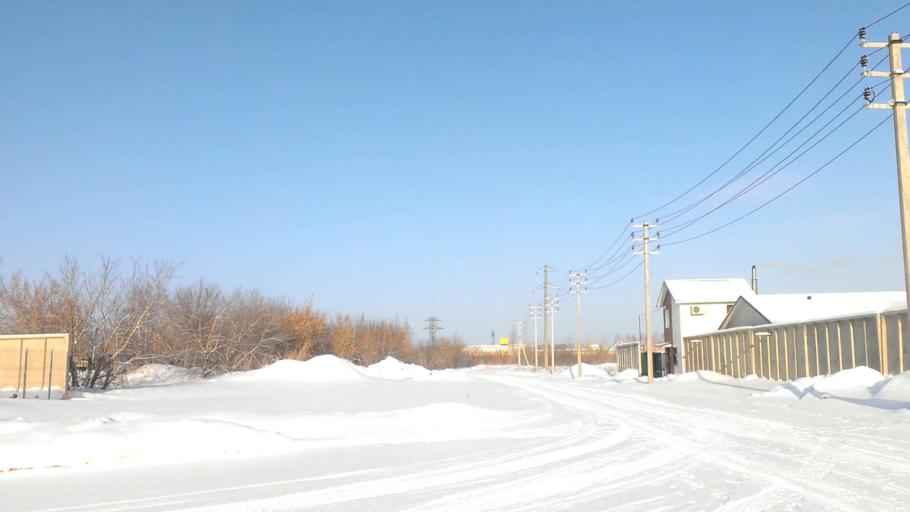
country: RU
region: Altai Krai
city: Novosilikatnyy
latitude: 53.3437
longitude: 83.6298
